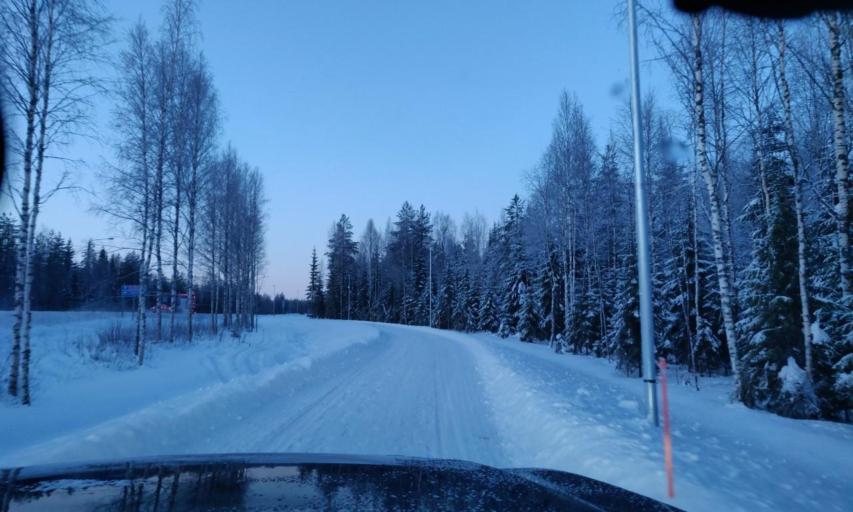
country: FI
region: Kainuu
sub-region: Kajaani
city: Paltamo
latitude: 64.2932
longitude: 27.9786
